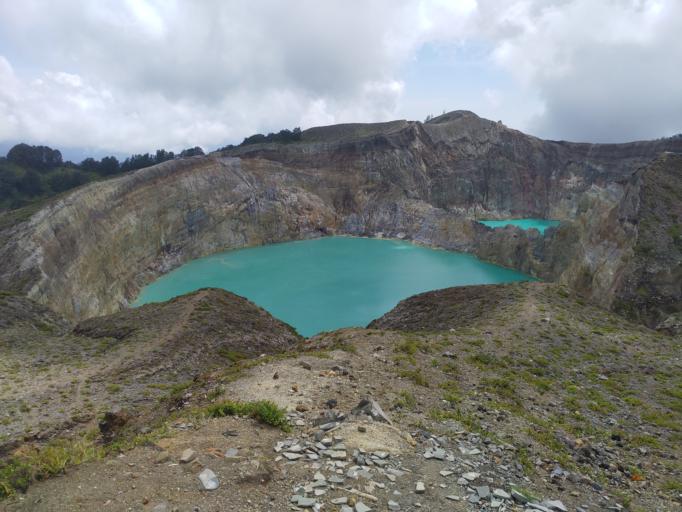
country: ID
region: East Nusa Tenggara
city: Koanara
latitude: -8.7654
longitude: 121.8123
